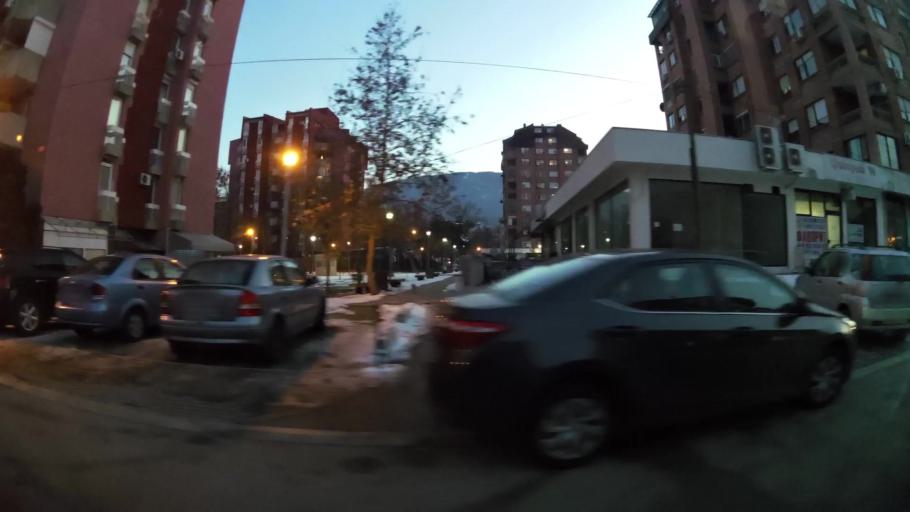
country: MK
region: Karpos
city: Skopje
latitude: 41.9976
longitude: 21.4094
